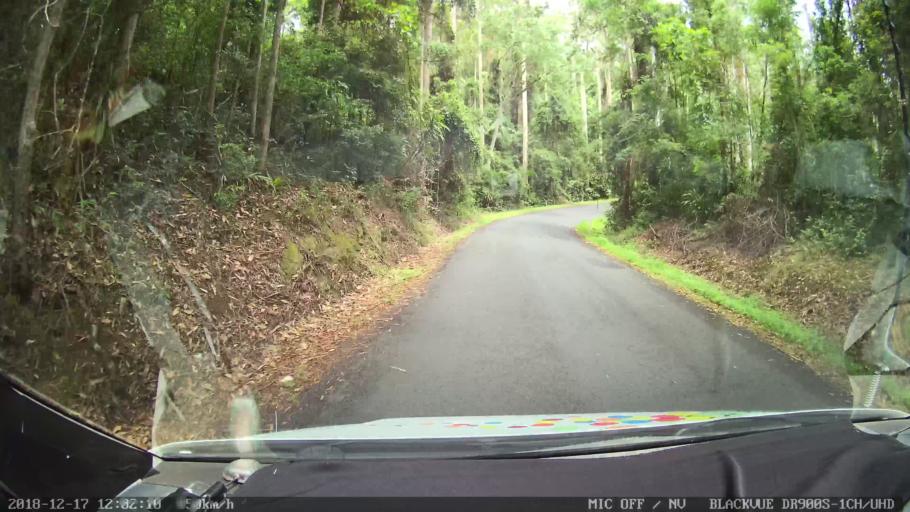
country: AU
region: New South Wales
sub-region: Kyogle
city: Kyogle
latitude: -28.5179
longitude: 152.5684
